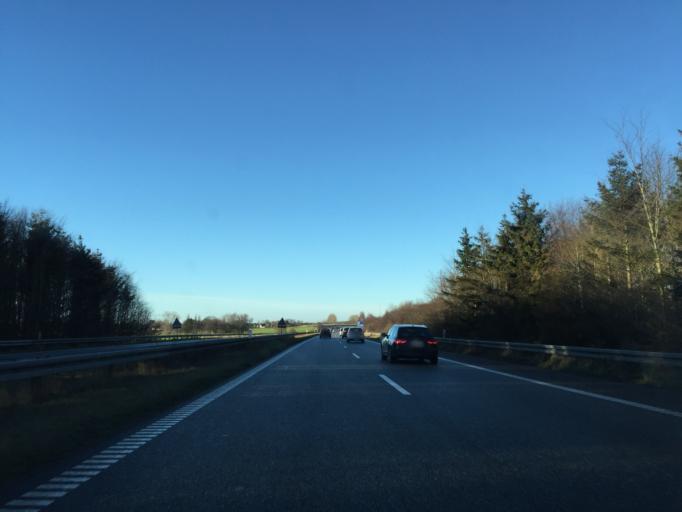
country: DK
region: South Denmark
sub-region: Nyborg Kommune
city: Ullerslev
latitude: 55.3451
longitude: 10.6229
